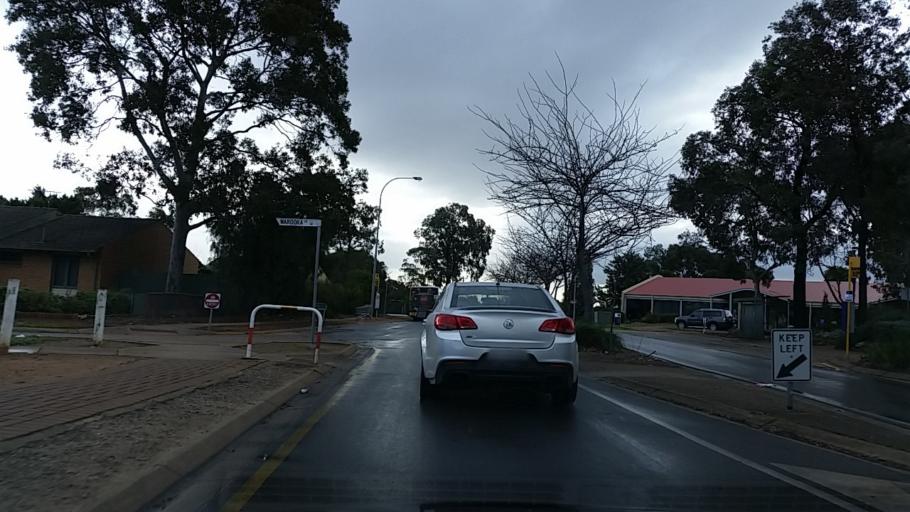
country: AU
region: South Australia
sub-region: Playford
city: Smithfield
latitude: -34.6846
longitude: 138.6890
